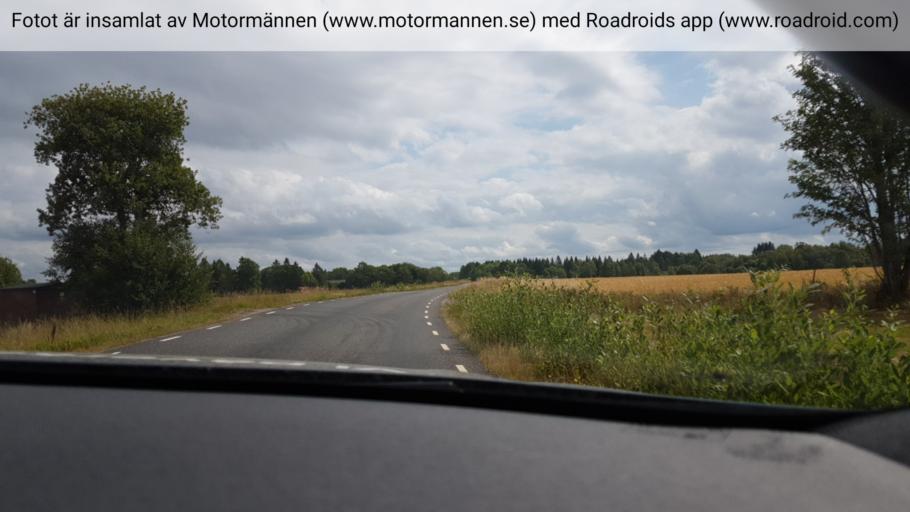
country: SE
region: Vaestra Goetaland
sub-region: Falkopings Kommun
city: Floby
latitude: 58.1265
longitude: 13.3741
